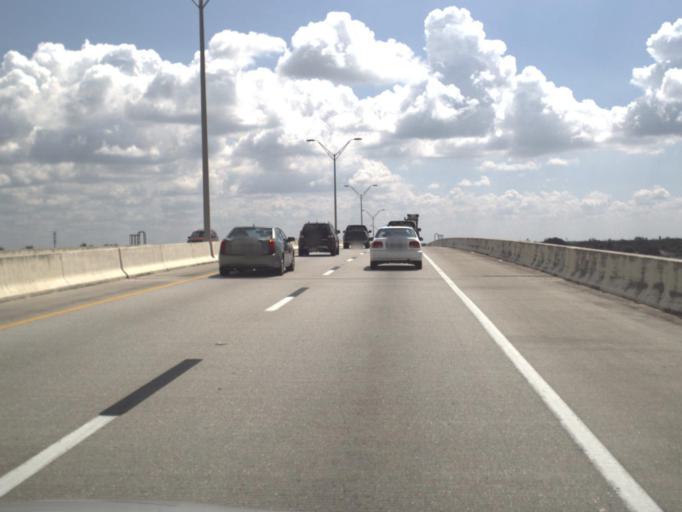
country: US
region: Florida
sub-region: Lee County
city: Whiskey Creek
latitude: 26.6015
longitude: -81.9016
